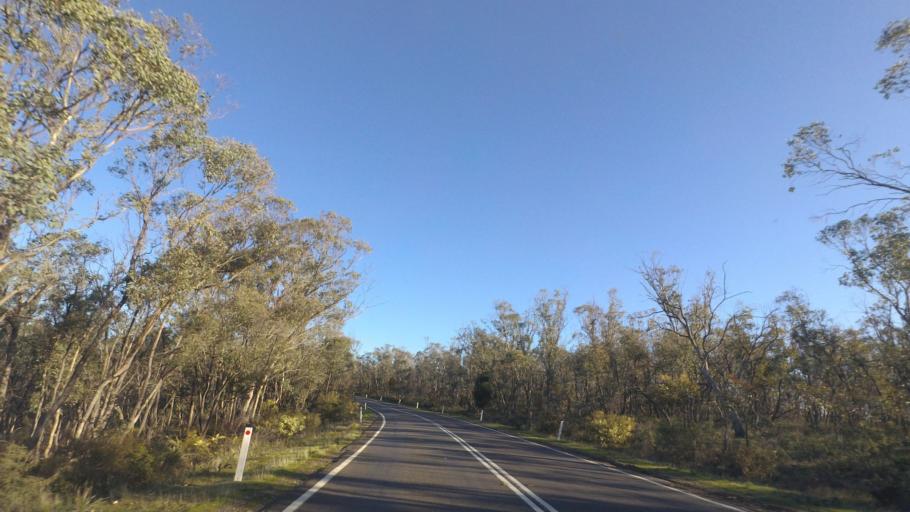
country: AU
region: Victoria
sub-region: Greater Bendigo
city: Kennington
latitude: -36.9237
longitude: 144.4900
